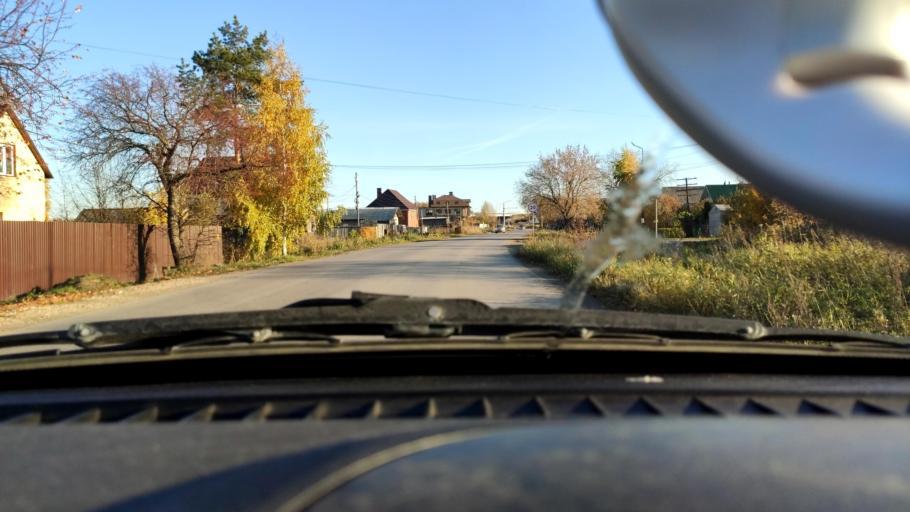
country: RU
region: Perm
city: Froly
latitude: 57.8831
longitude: 56.2604
